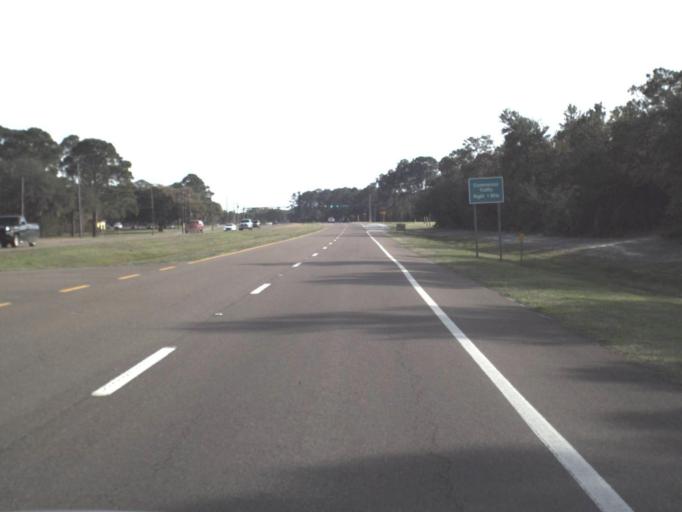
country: US
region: Florida
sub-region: Bay County
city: Tyndall Air Force Base
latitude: 30.0914
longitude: -85.6112
